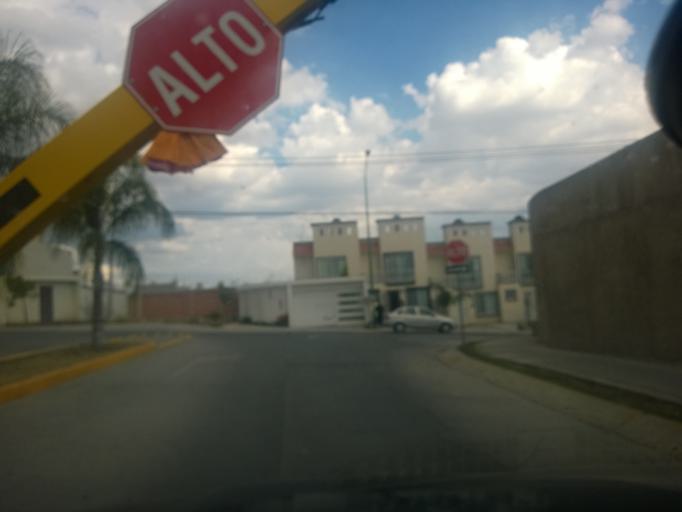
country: MX
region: Guanajuato
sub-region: Leon
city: La Ermita
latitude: 21.1564
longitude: -101.7444
